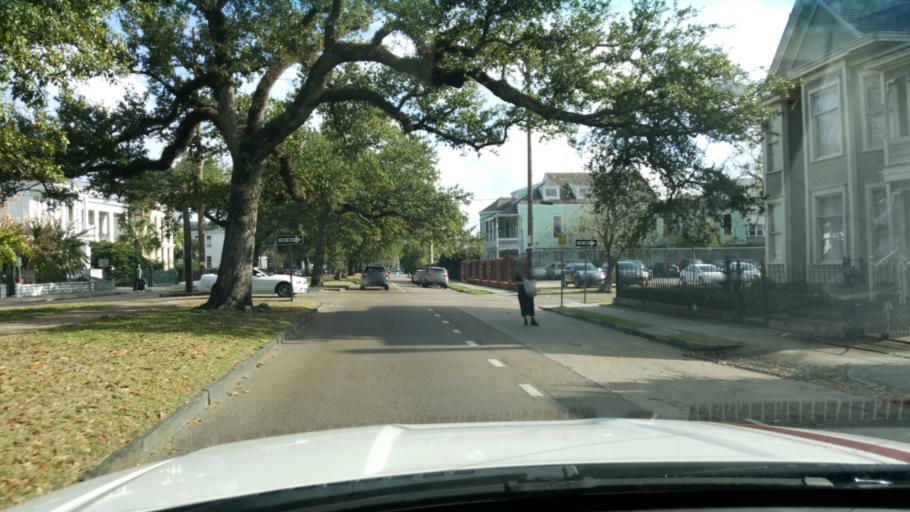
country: US
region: Louisiana
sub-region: Orleans Parish
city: New Orleans
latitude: 29.9708
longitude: -90.0708
